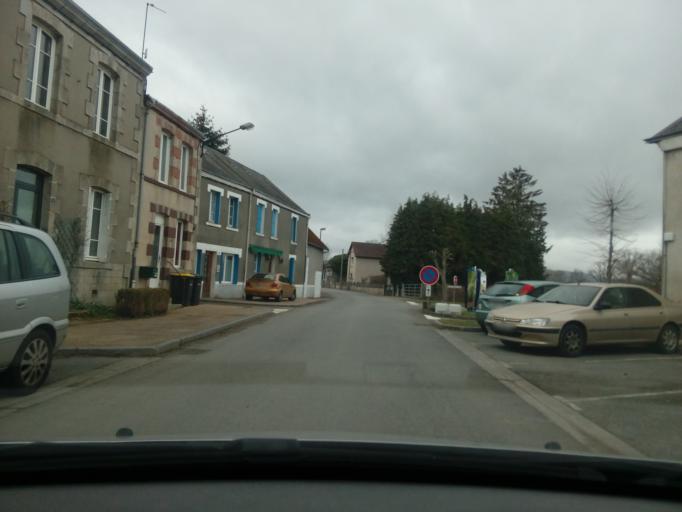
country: FR
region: Limousin
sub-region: Departement de la Creuse
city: Ajain
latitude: 46.1666
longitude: 1.9619
